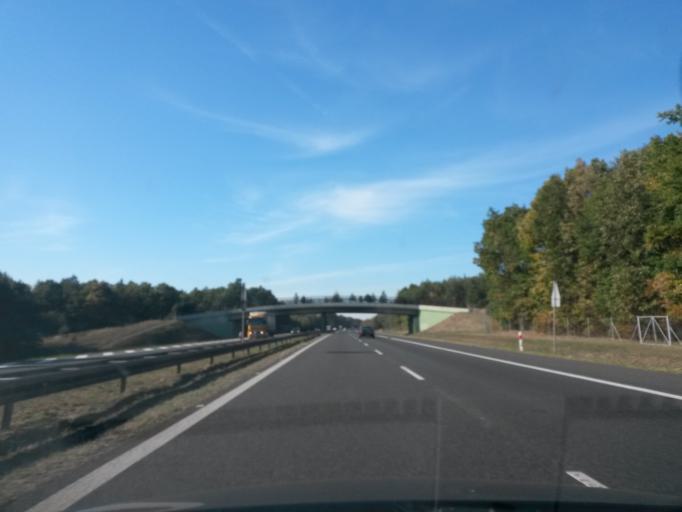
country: PL
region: Opole Voivodeship
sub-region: Powiat opolski
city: Niemodlin
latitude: 50.6850
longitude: 17.6397
